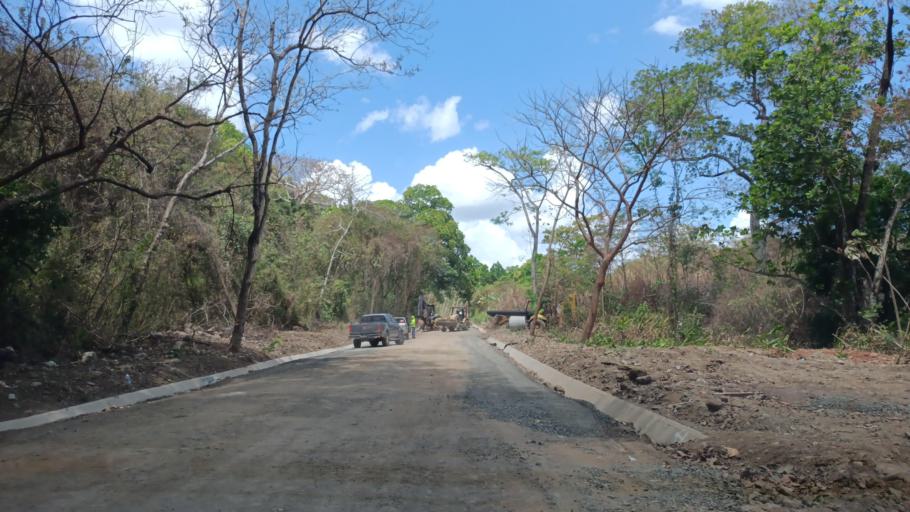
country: PA
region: Panama
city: Las Cumbres
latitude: 9.0651
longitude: -79.5673
